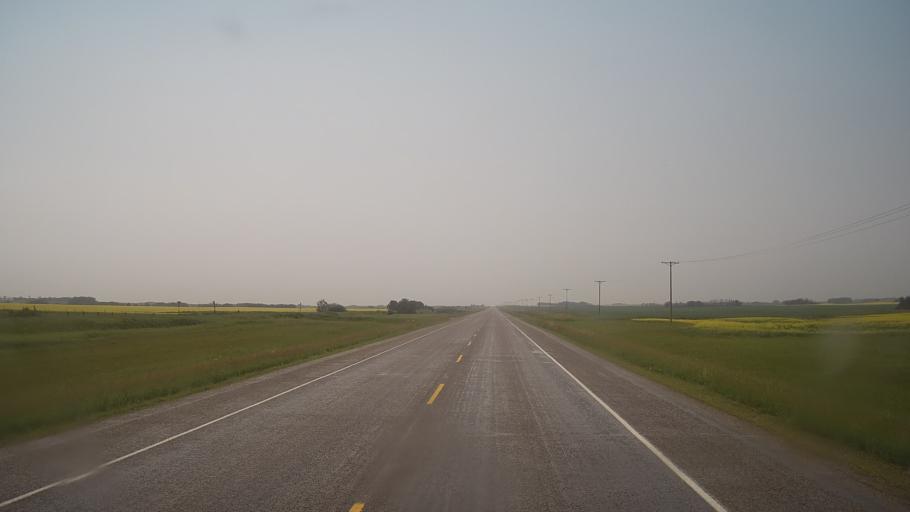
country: CA
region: Saskatchewan
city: Biggar
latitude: 52.1521
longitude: -108.2383
